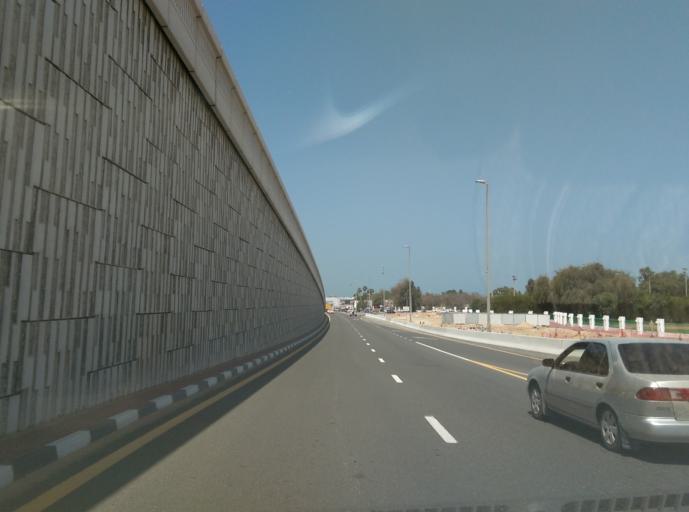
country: AE
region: Dubai
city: Dubai
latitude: 25.1813
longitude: 55.2485
